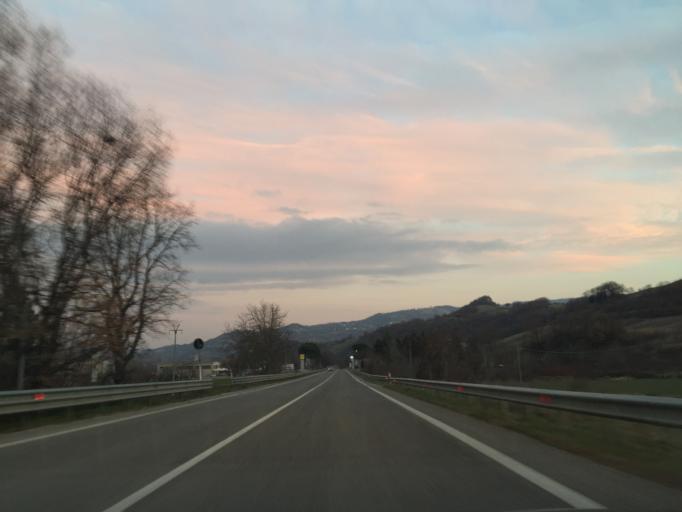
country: IT
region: Molise
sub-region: Provincia di Campobasso
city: Gambatesa
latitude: 41.5369
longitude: 14.8816
